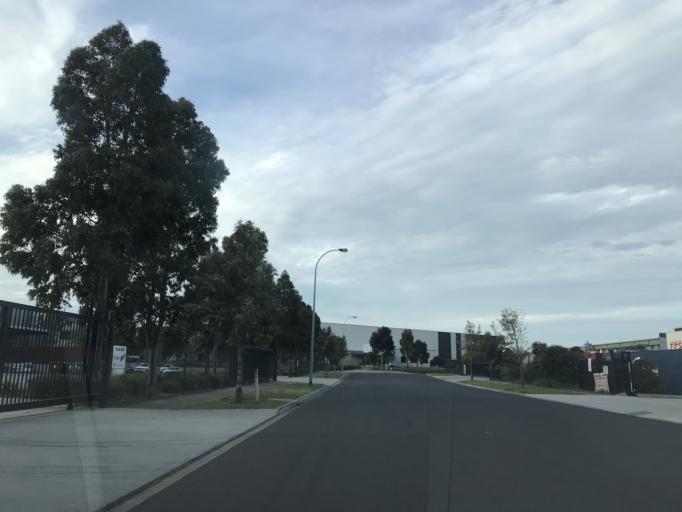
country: AU
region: Victoria
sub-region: Brimbank
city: Derrimut
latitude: -37.8059
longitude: 144.7650
